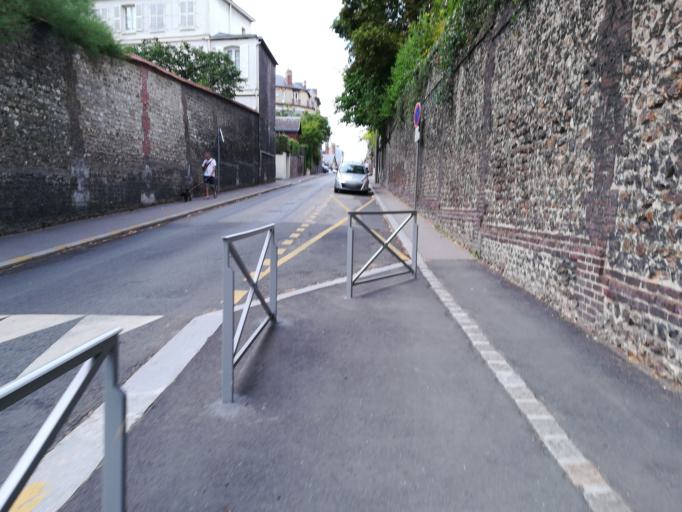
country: FR
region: Haute-Normandie
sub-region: Departement de la Seine-Maritime
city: Rouen
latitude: 49.4512
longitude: 1.0931
